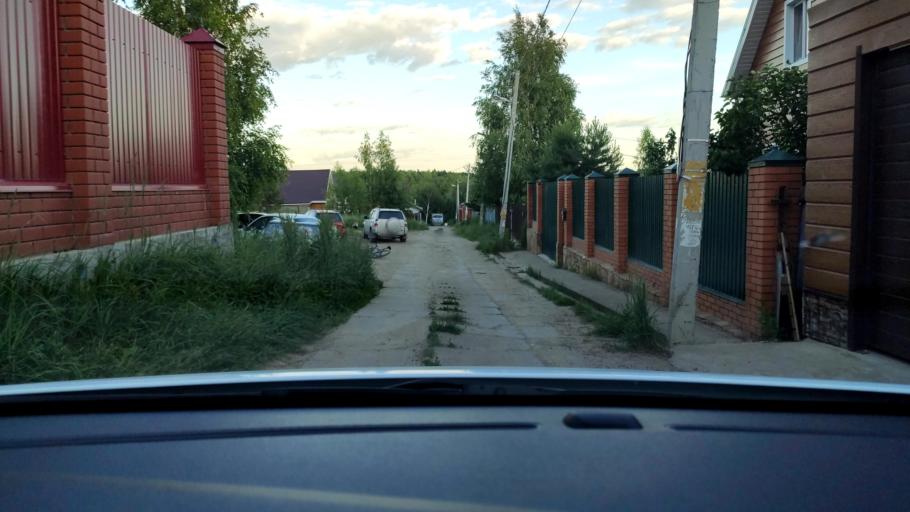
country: RU
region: Tatarstan
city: Stolbishchi
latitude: 55.7597
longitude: 49.3029
